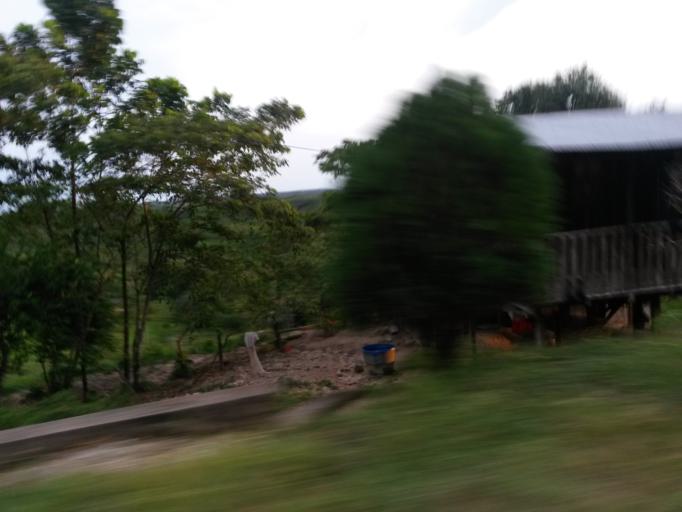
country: CO
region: Putumayo
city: Puerto Guzman
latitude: 1.1372
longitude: -76.2760
